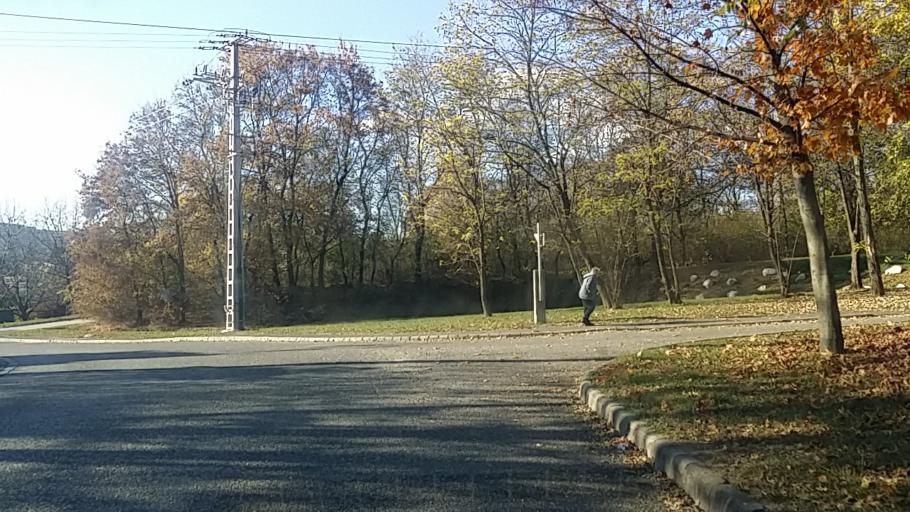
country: HU
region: Pest
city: Pilisszanto
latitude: 47.6700
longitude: 18.8849
